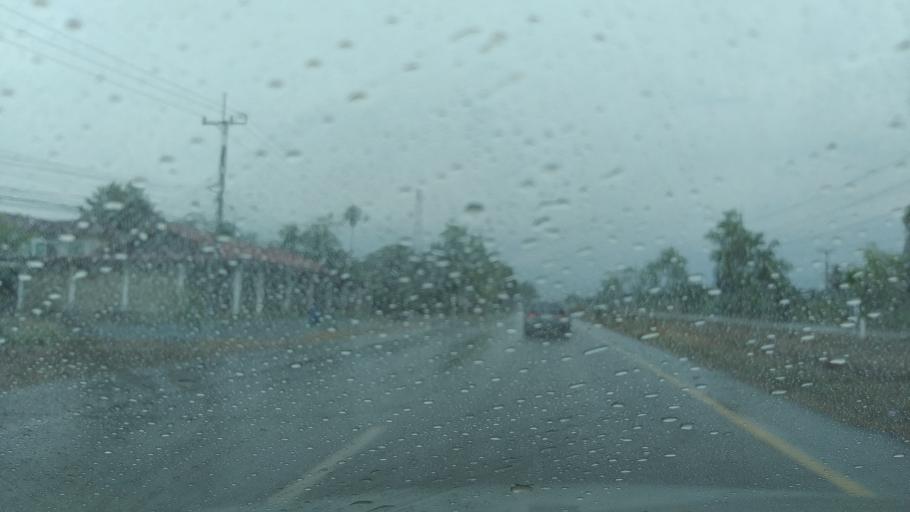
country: TH
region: Trat
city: Khao Saming
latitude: 12.3991
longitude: 102.3482
